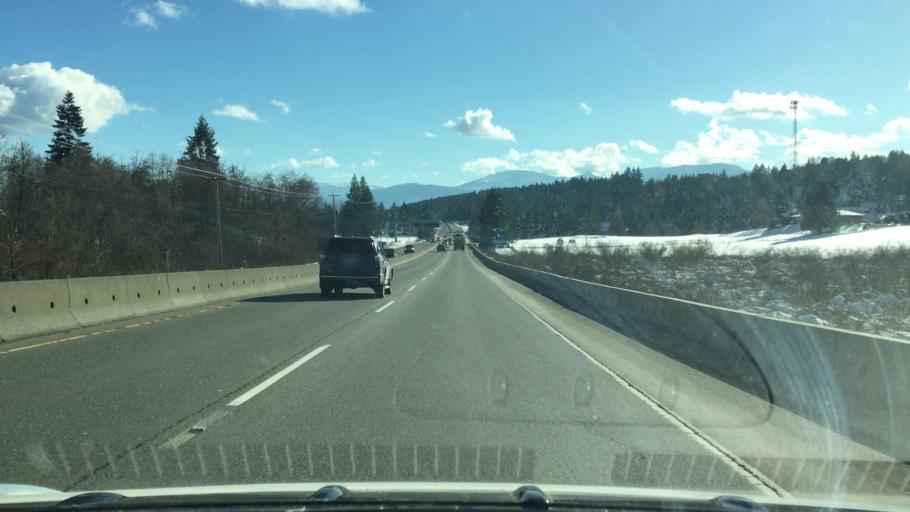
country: CA
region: British Columbia
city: Nanaimo
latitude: 49.0849
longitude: -123.8831
